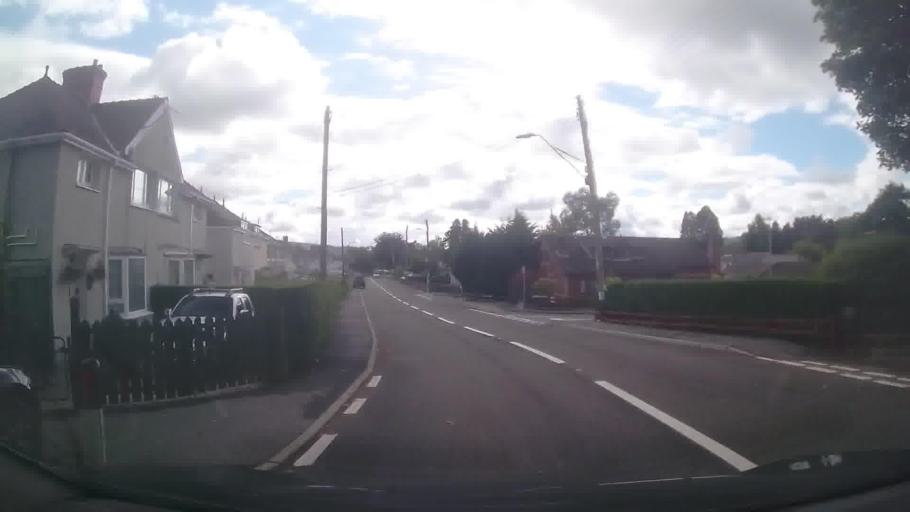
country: GB
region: Wales
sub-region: Carmarthenshire
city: Llandovery
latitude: 51.9992
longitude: -3.7957
